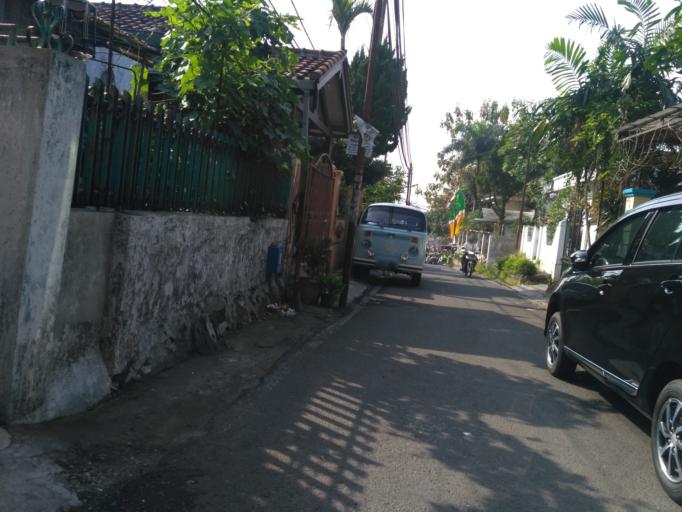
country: ID
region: East Java
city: Malang
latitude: -7.9795
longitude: 112.6212
